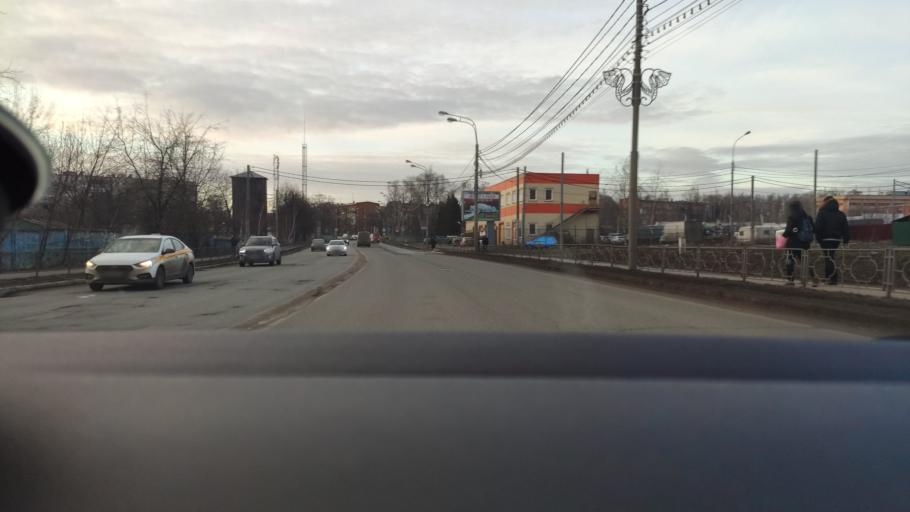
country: RU
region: Moskovskaya
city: Vidnoye
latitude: 55.5470
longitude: 37.7189
